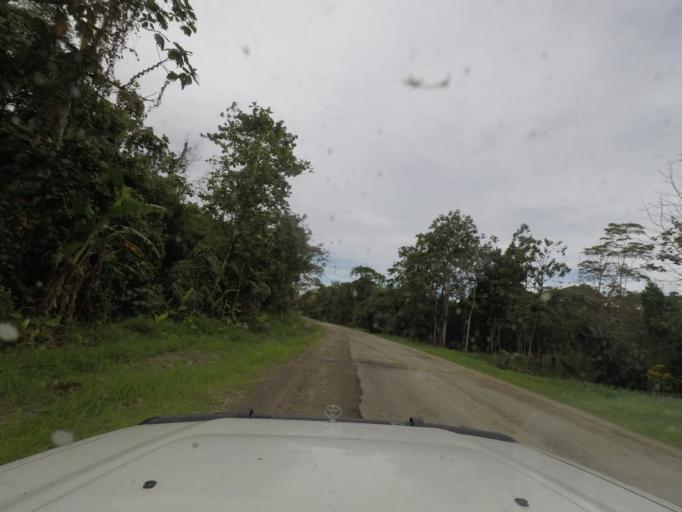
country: PG
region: Eastern Highlands
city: Goroka
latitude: -5.6489
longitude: 145.4906
